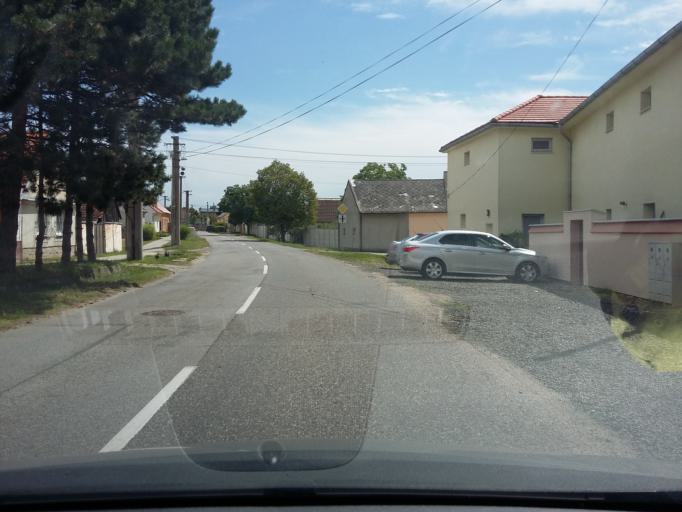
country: SK
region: Bratislavsky
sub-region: Okres Malacky
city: Malacky
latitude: 48.5022
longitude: 16.9982
